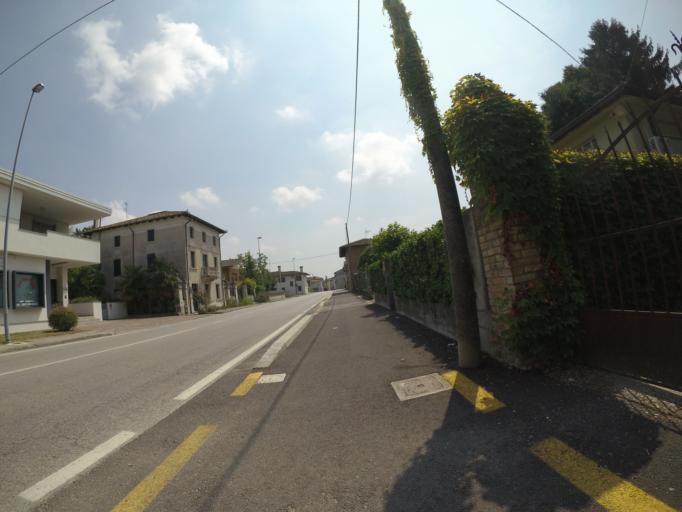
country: IT
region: Friuli Venezia Giulia
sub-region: Provincia di Udine
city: Teor
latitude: 45.8577
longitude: 13.0548
